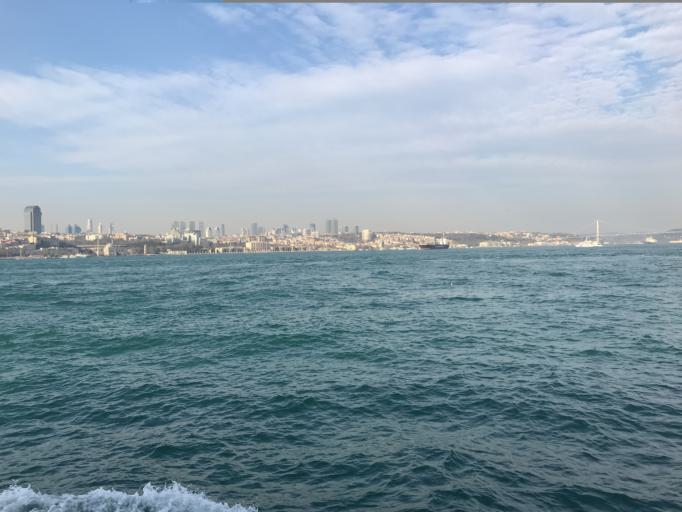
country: TR
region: Istanbul
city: Eminoenue
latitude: 41.0220
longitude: 28.9969
